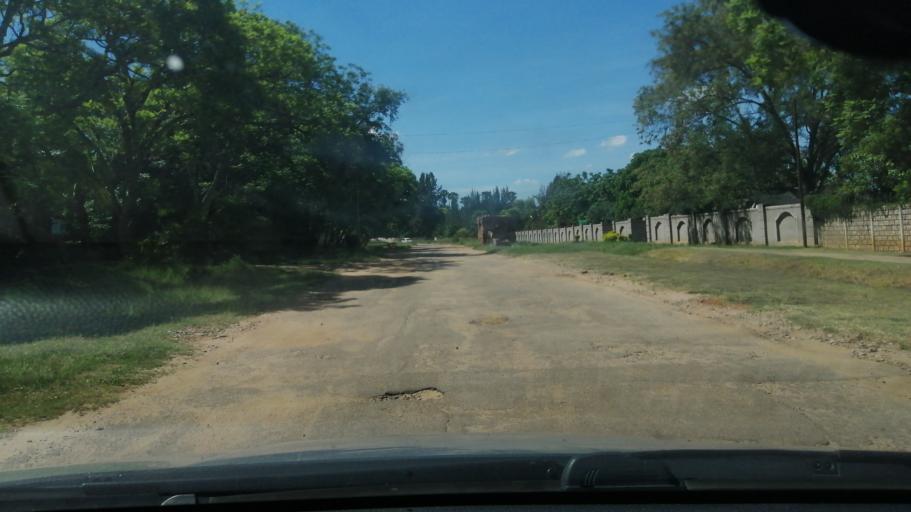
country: ZW
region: Harare
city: Harare
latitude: -17.8156
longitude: 31.1287
